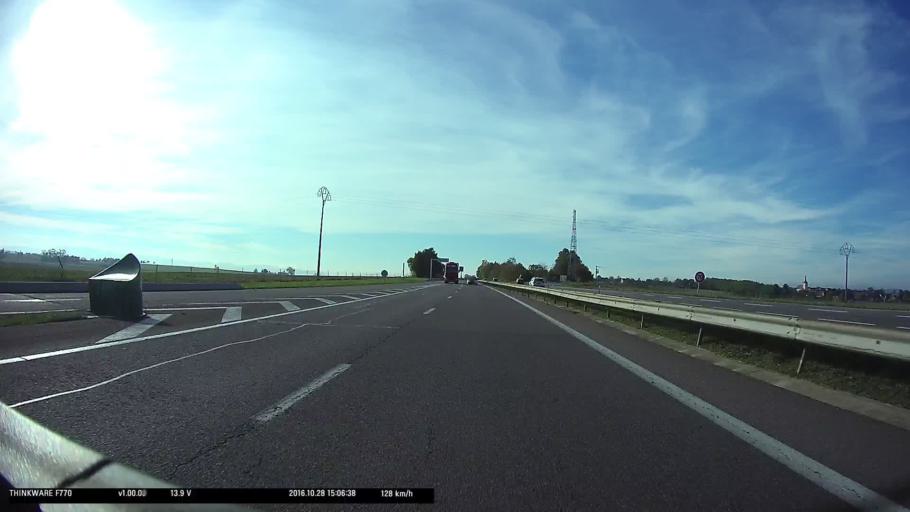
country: FR
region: Alsace
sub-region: Departement du Bas-Rhin
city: Dettwiller
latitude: 48.7706
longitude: 7.4914
